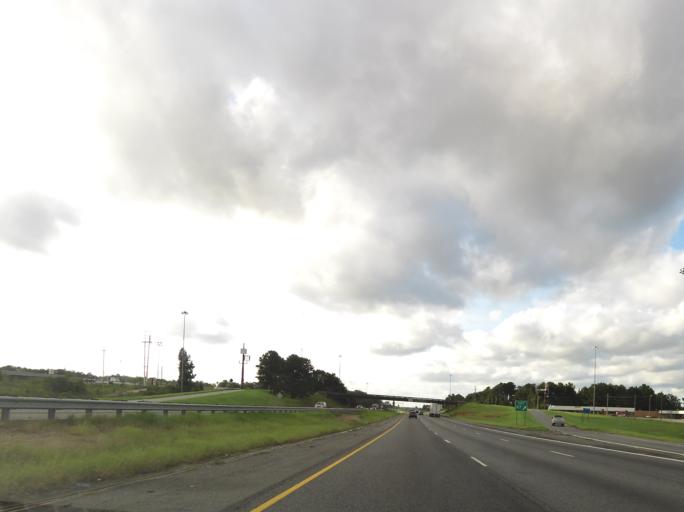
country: US
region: Georgia
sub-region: Crisp County
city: Cordele
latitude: 31.9045
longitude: -83.7366
